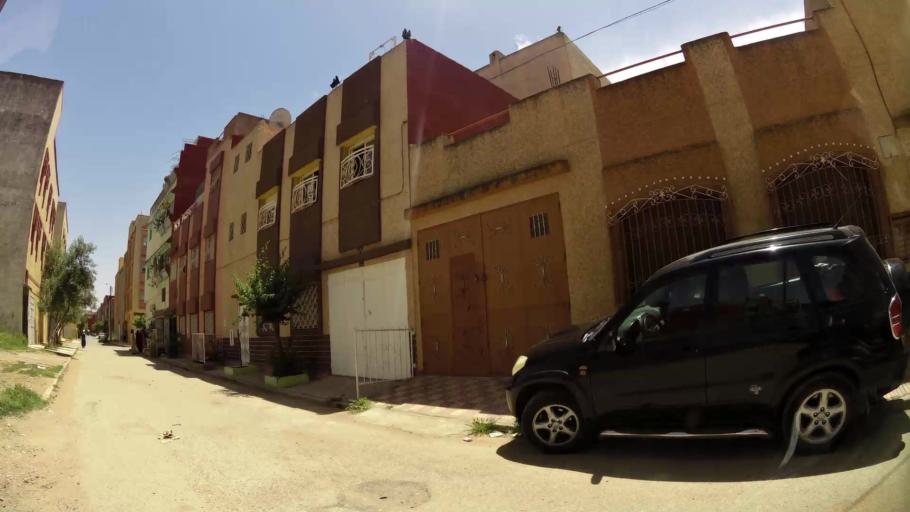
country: MA
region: Rabat-Sale-Zemmour-Zaer
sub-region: Khemisset
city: Khemisset
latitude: 33.8248
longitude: -6.0818
